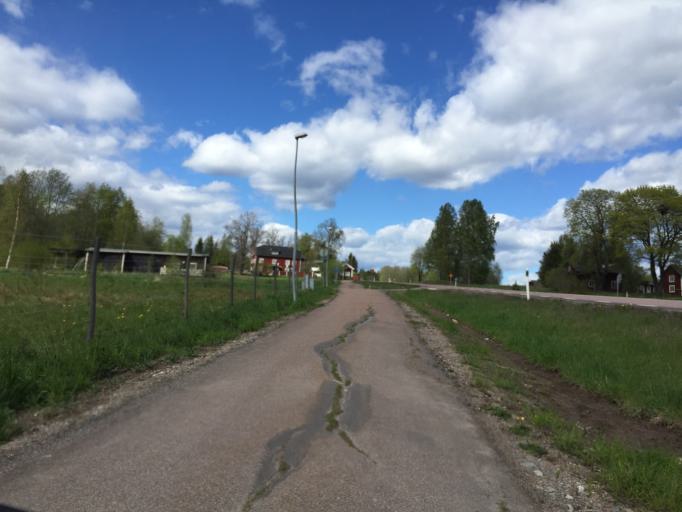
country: SE
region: Dalarna
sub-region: Ludvika Kommun
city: Ludvika
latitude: 60.1951
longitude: 15.2146
